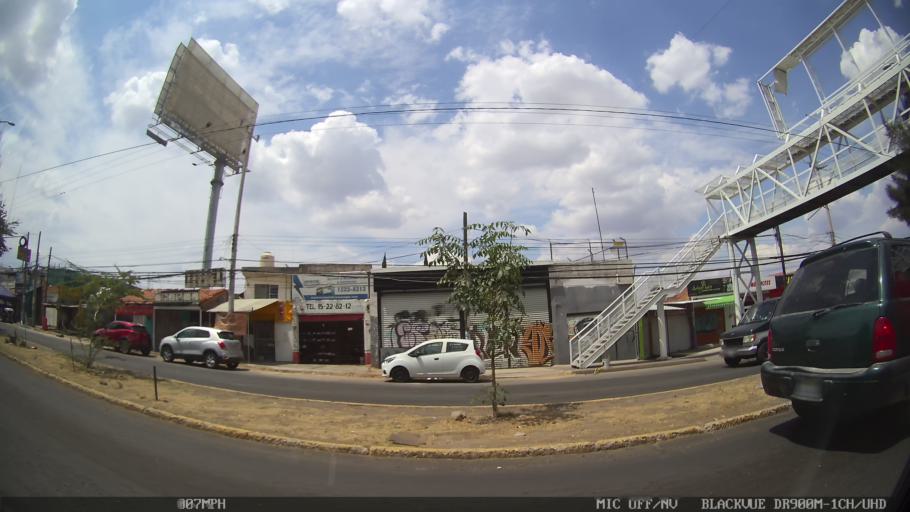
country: MX
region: Jalisco
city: Tlaquepaque
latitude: 20.6333
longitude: -103.2708
